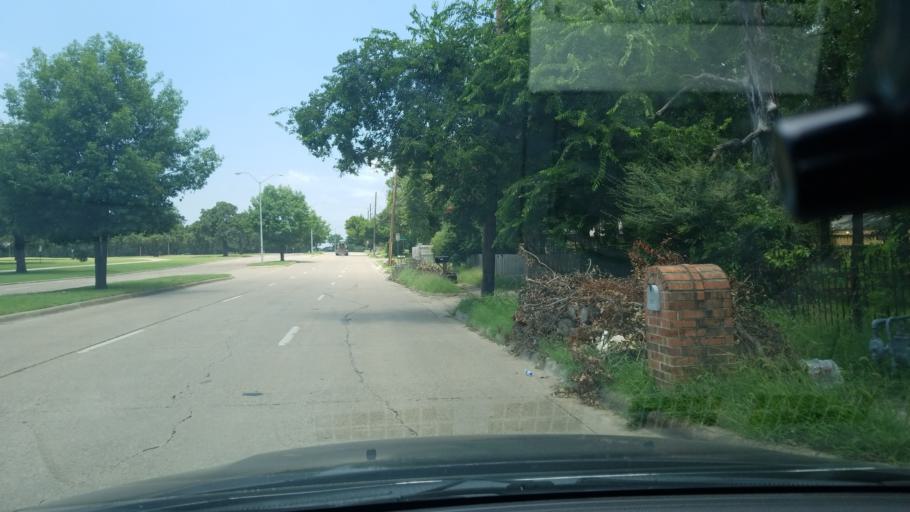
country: US
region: Texas
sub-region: Dallas County
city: Balch Springs
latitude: 32.7158
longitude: -96.6655
